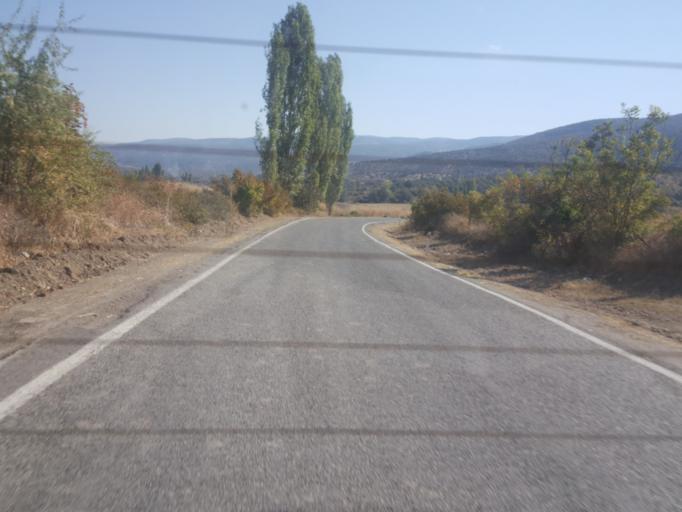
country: TR
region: Kastamonu
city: Tosya
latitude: 40.9928
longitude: 34.1190
